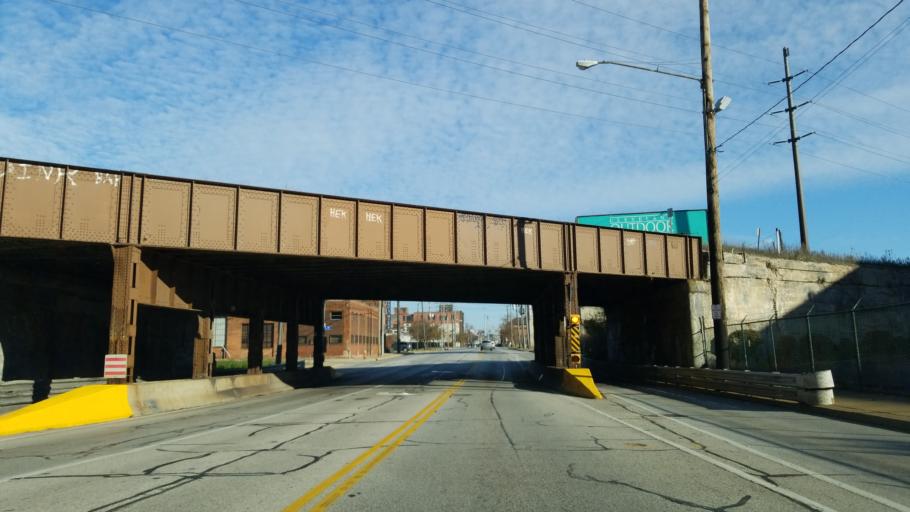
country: US
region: Ohio
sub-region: Cuyahoga County
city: Cleveland
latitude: 41.5016
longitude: -81.6490
